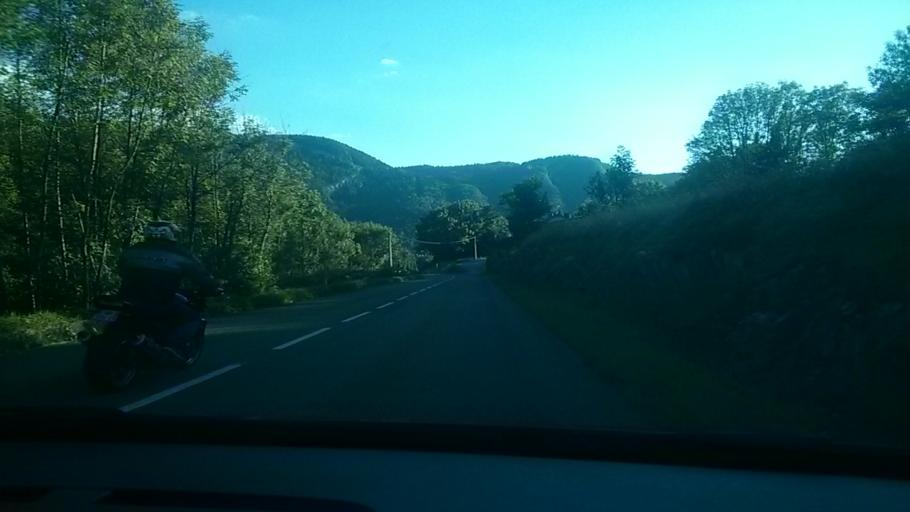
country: FR
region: Franche-Comte
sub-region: Departement du Jura
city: Saint-Claude
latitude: 46.3651
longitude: 5.9129
